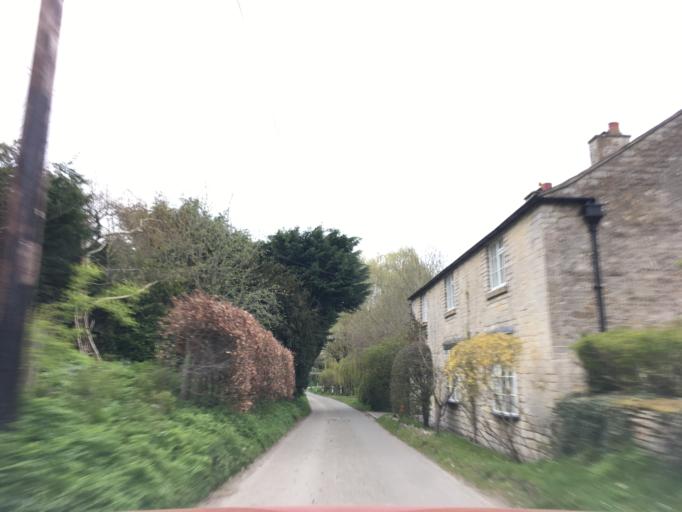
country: GB
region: England
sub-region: Gloucestershire
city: Wotton-under-Edge
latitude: 51.5996
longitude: -2.3082
